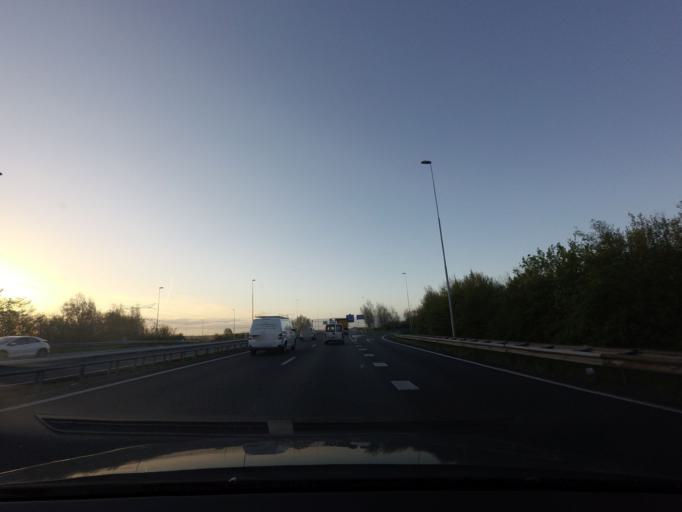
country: NL
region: North Holland
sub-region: Gemeente Zaanstad
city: Zaandam
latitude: 52.4579
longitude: 4.8379
